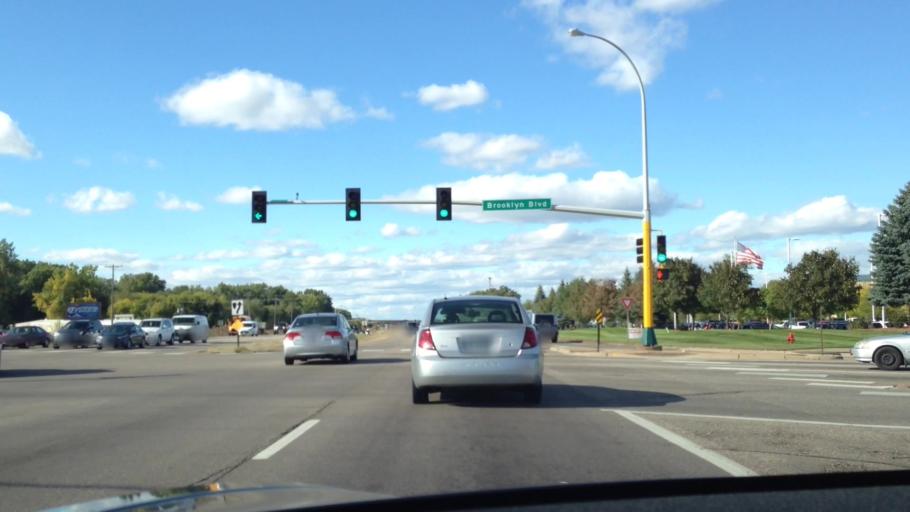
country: US
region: Minnesota
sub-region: Hennepin County
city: Brooklyn Park
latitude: 45.0944
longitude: -93.3839
